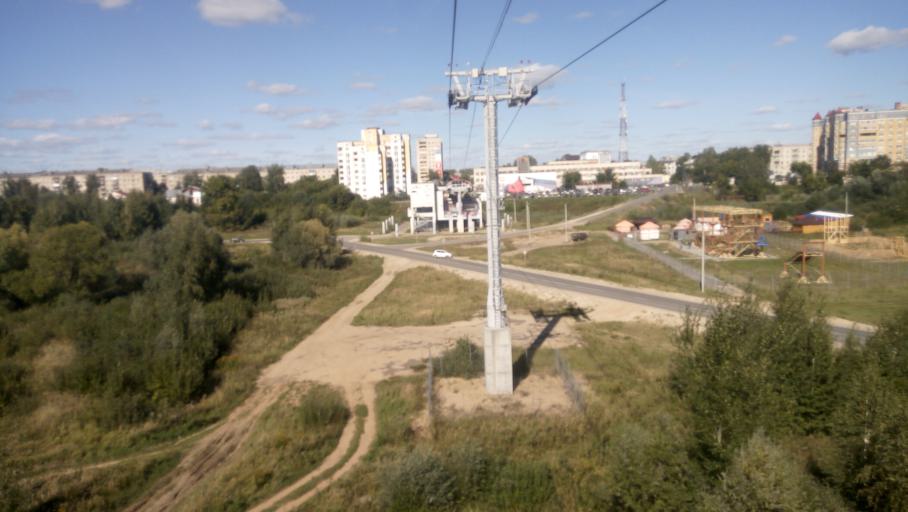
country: RU
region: Nizjnij Novgorod
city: Bor
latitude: 56.3523
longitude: 44.0598
